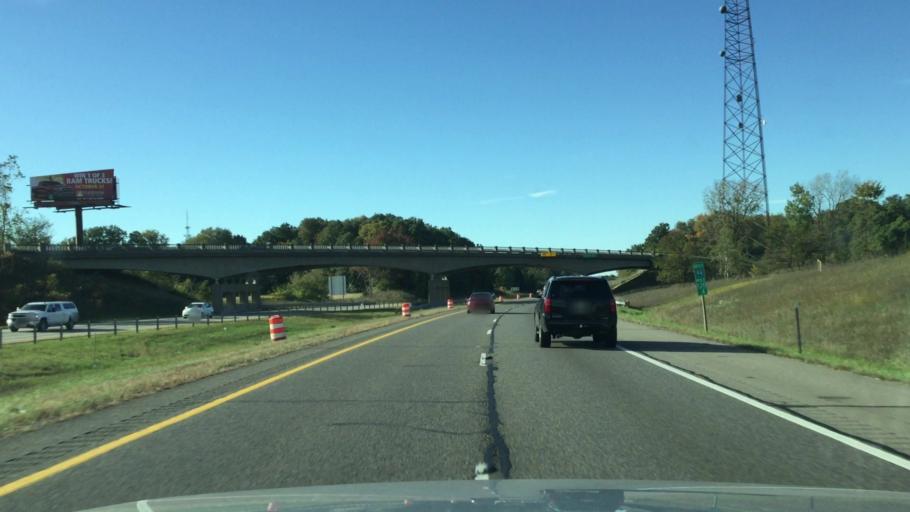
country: US
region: Michigan
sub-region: Calhoun County
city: Albion
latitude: 42.2671
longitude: -84.7749
